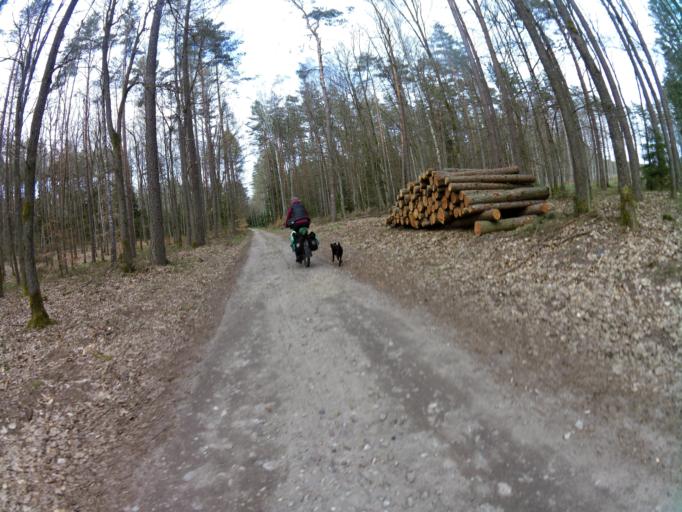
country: PL
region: West Pomeranian Voivodeship
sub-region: Powiat szczecinecki
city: Szczecinek
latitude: 53.8288
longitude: 16.6560
